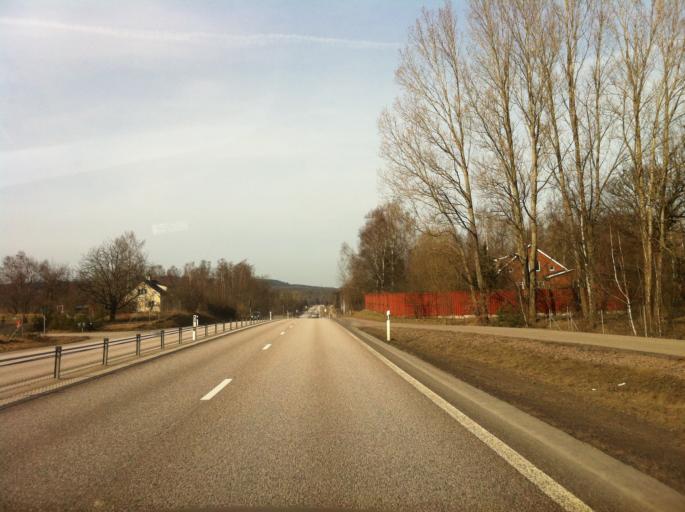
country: SE
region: Vaestra Goetaland
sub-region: Skovde Kommun
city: Stopen
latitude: 58.4329
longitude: 13.8611
